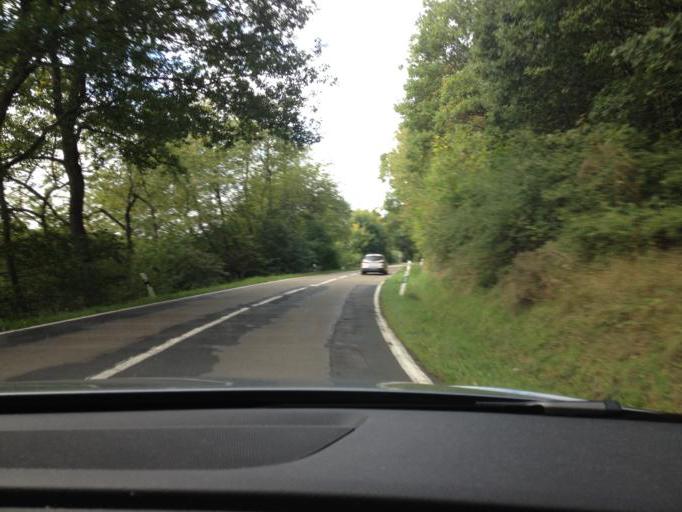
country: DE
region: Saarland
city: Mainzweiler
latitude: 49.4073
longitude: 7.1353
